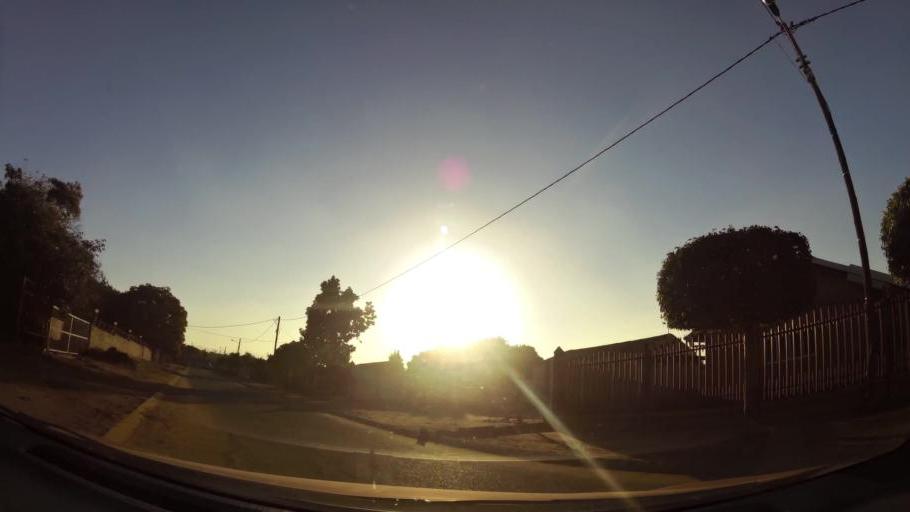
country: ZA
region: North-West
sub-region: Bojanala Platinum District Municipality
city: Rustenburg
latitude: -25.6314
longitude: 27.2138
